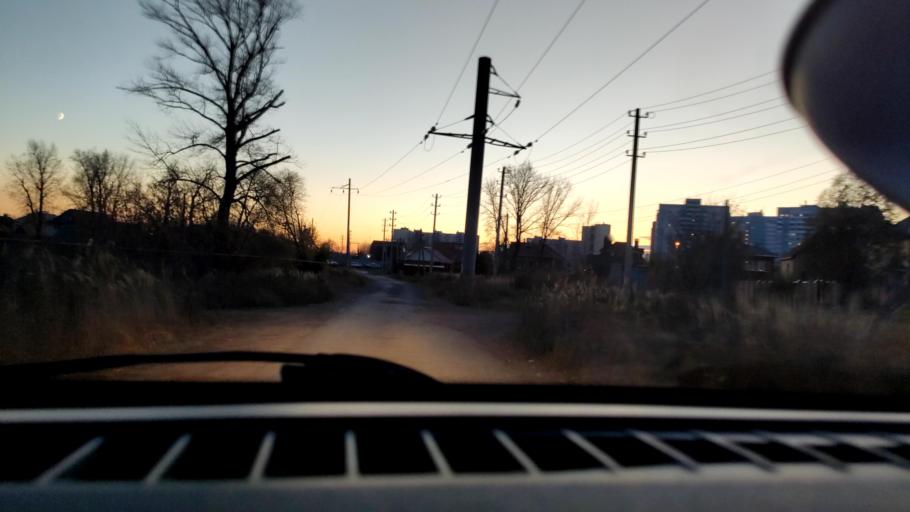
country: RU
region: Samara
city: Samara
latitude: 53.1485
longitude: 50.0870
